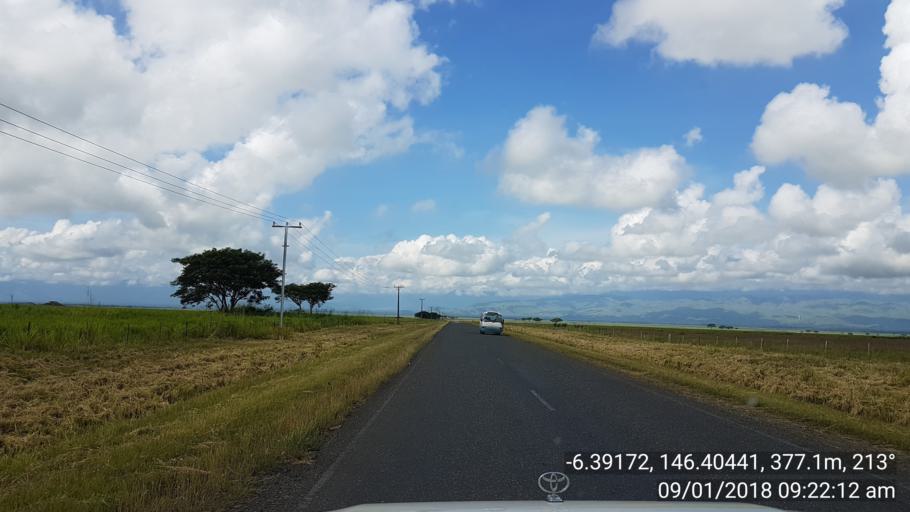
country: PG
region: Eastern Highlands
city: Kainantu
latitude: -6.3915
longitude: 146.4045
